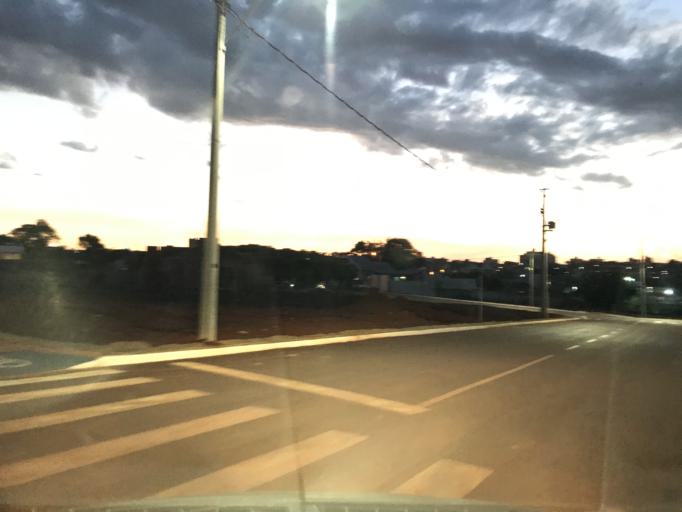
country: BR
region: Parana
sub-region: Palotina
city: Palotina
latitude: -24.2910
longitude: -53.8296
